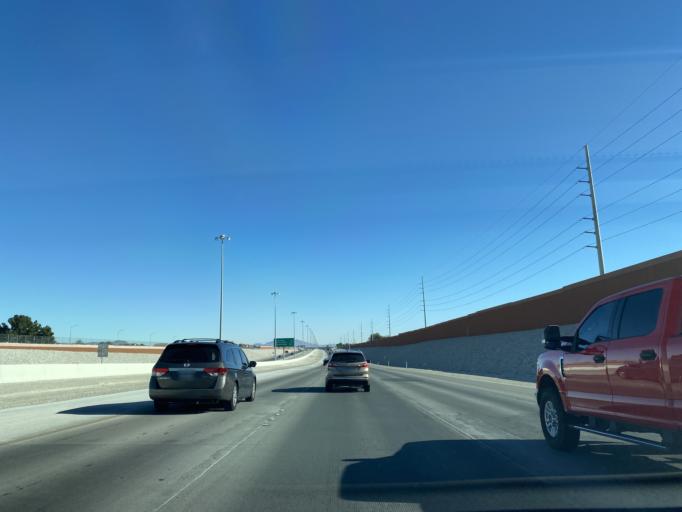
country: US
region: Nevada
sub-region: Clark County
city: Las Vegas
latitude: 36.2750
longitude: -115.2454
